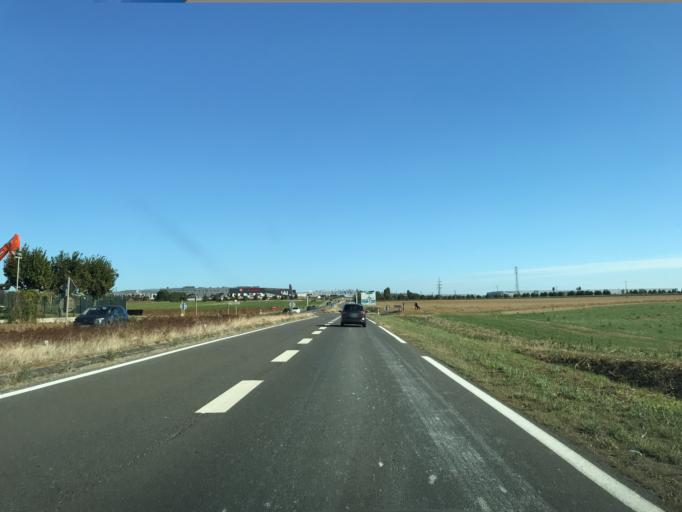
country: FR
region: Ile-de-France
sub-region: Departement de Seine-et-Marne
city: Chauconin-Neufmontiers
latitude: 48.9576
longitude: 2.8480
